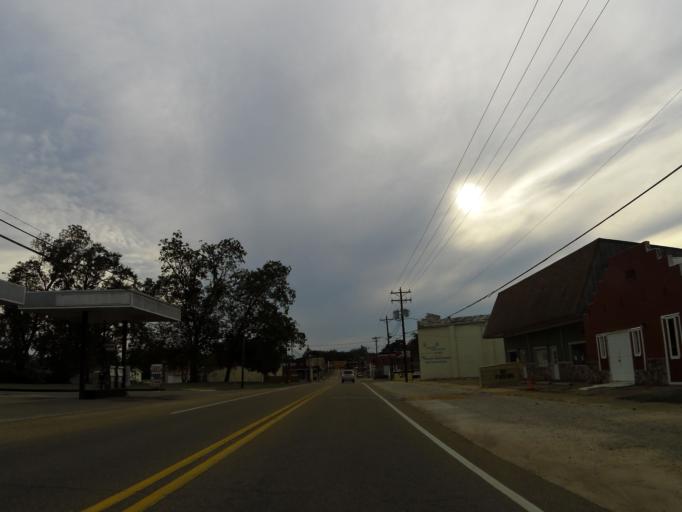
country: US
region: Alabama
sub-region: Monroe County
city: Frisco City
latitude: 31.4342
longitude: -87.3997
